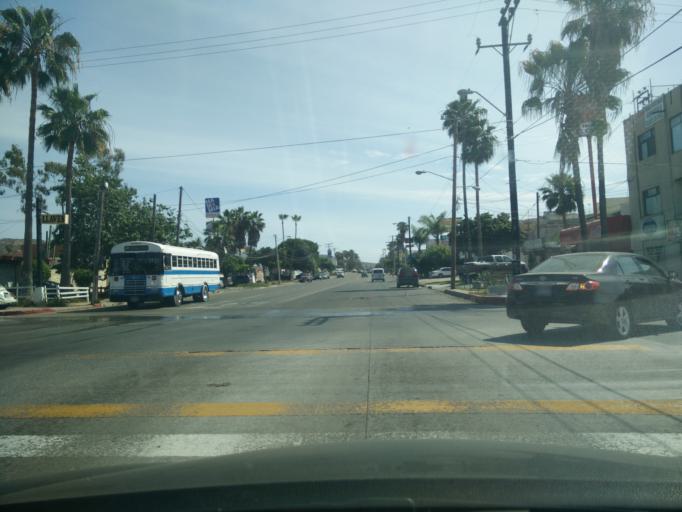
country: MX
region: Baja California
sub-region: Tijuana
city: La Esperanza [Granjas Familiares]
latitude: 32.5202
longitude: -117.1162
